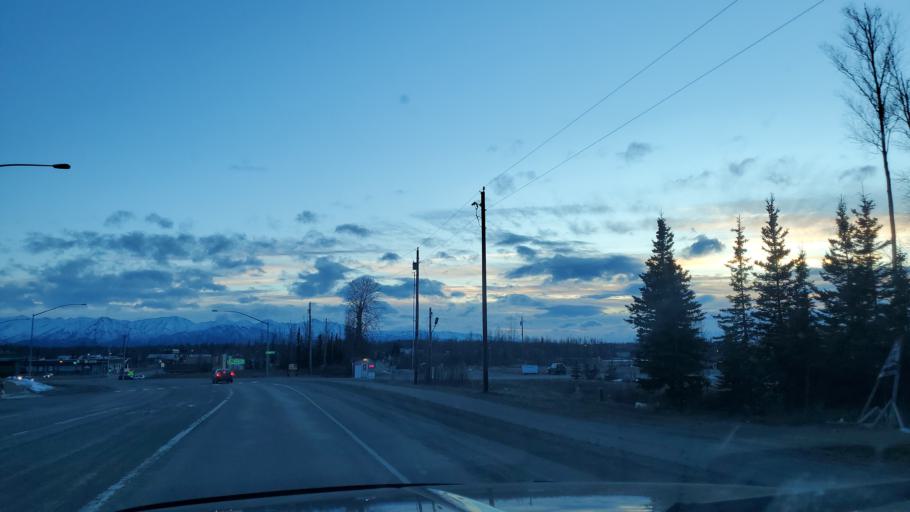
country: US
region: Alaska
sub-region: Matanuska-Susitna Borough
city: Wasilla
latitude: 61.5871
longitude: -149.4434
